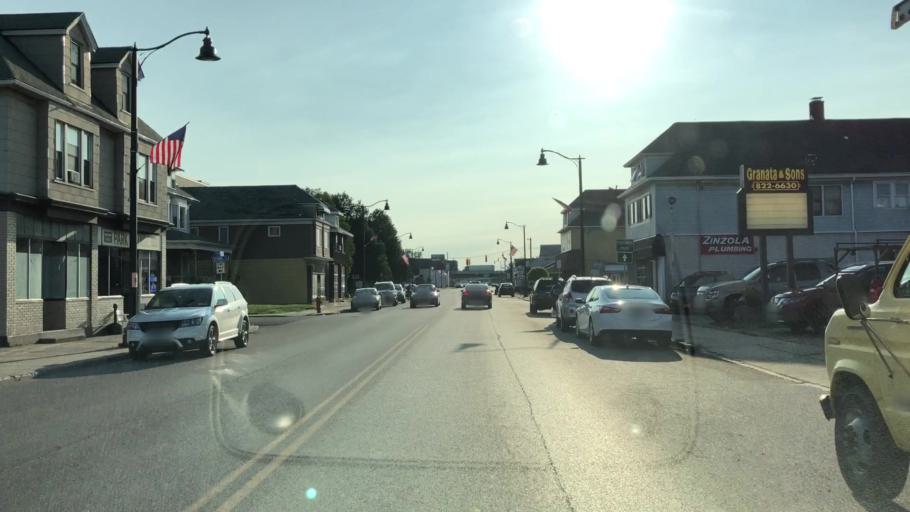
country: US
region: New York
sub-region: Erie County
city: West Seneca
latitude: 42.8719
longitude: -78.8110
